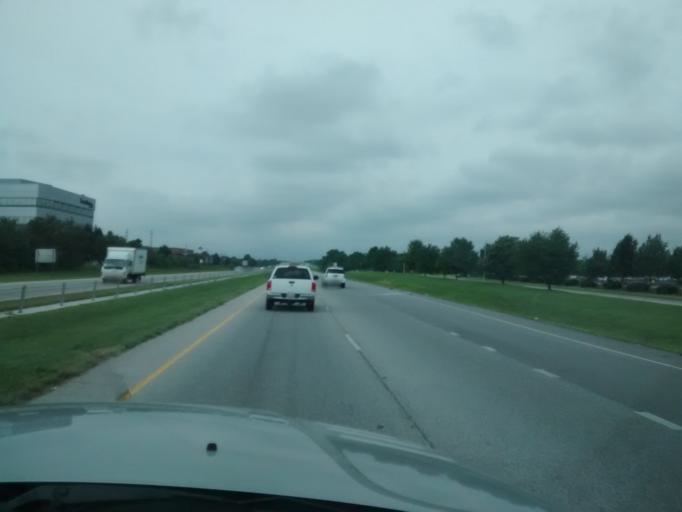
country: US
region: Arkansas
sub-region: Washington County
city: Johnson
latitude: 36.1154
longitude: -94.1514
